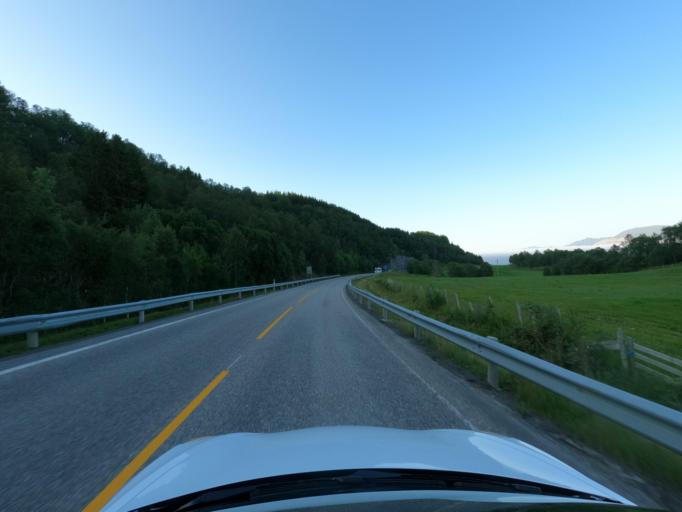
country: NO
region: Troms
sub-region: Harstad
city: Harstad
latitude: 68.7286
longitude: 16.5422
